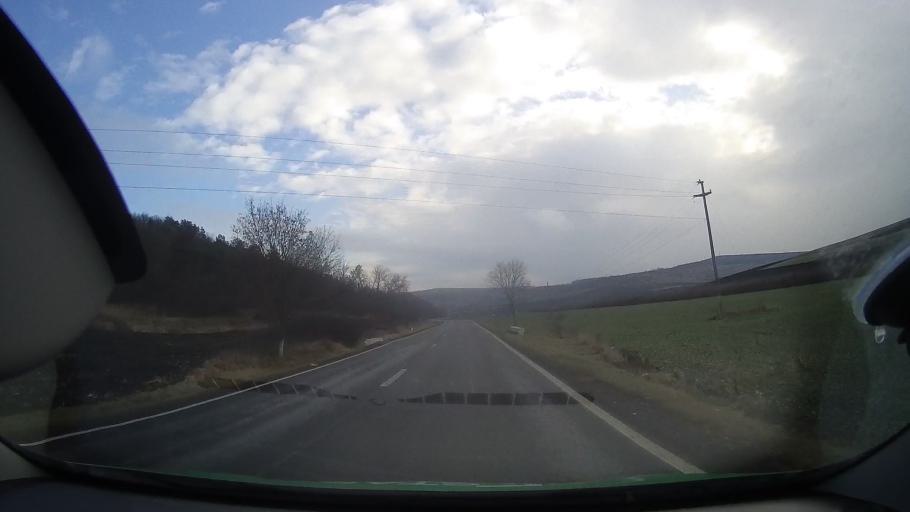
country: RO
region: Mures
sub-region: Comuna Cucerdea
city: Cucerdea
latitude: 46.3694
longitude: 24.2623
